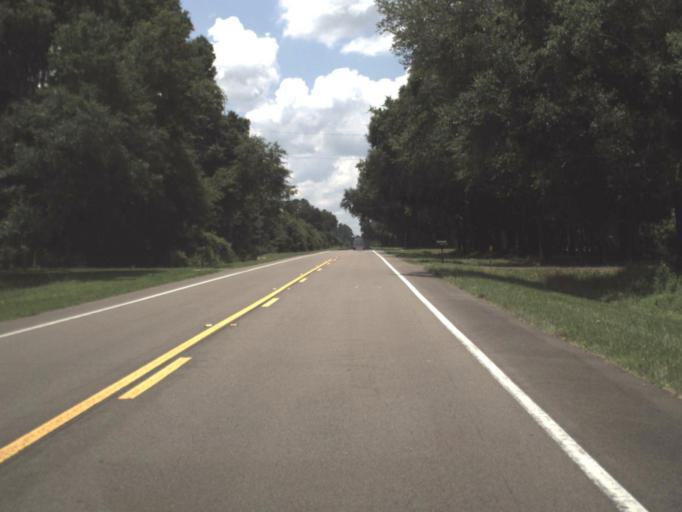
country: US
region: Florida
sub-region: Alachua County
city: Alachua
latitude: 29.8161
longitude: -82.3868
